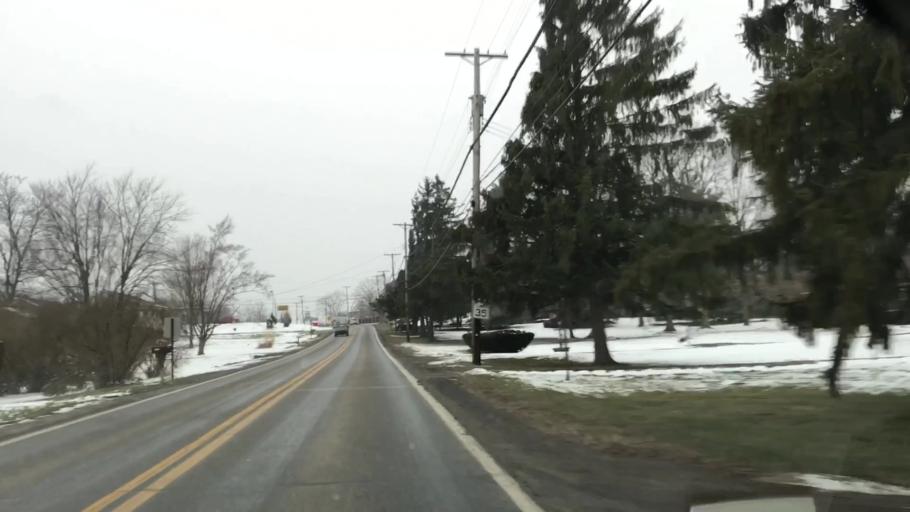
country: US
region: Pennsylvania
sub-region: Beaver County
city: Industry
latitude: 40.7025
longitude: -80.3977
